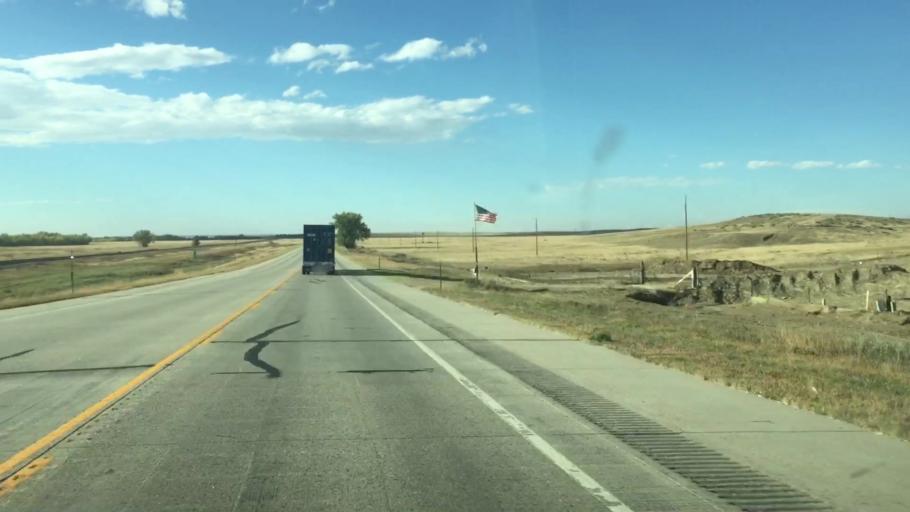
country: US
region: Colorado
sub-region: Lincoln County
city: Limon
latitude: 39.2159
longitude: -103.6027
